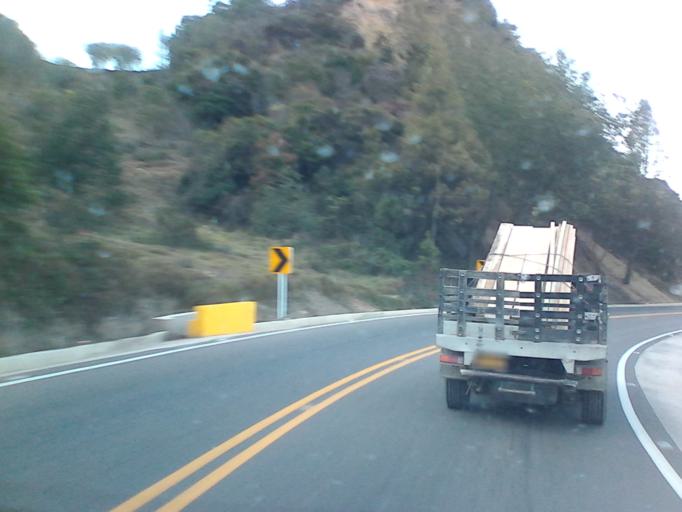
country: CO
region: Boyaca
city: Cucaita
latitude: 5.5566
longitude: -73.4311
